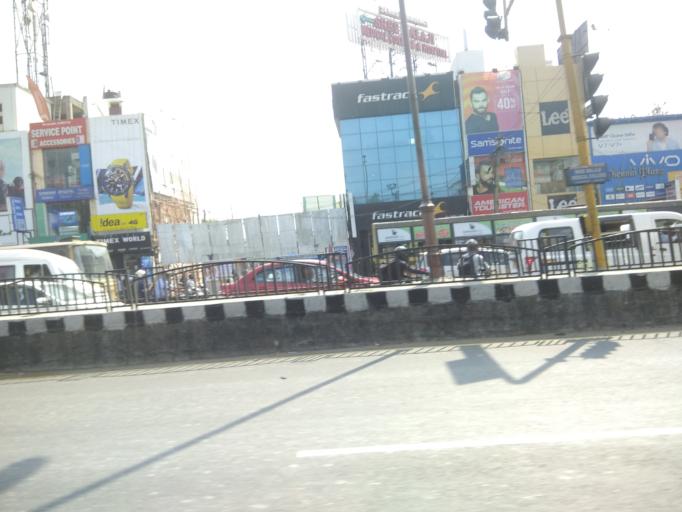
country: IN
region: Tamil Nadu
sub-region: Kancheepuram
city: Pallavaram
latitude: 12.9507
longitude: 80.1396
